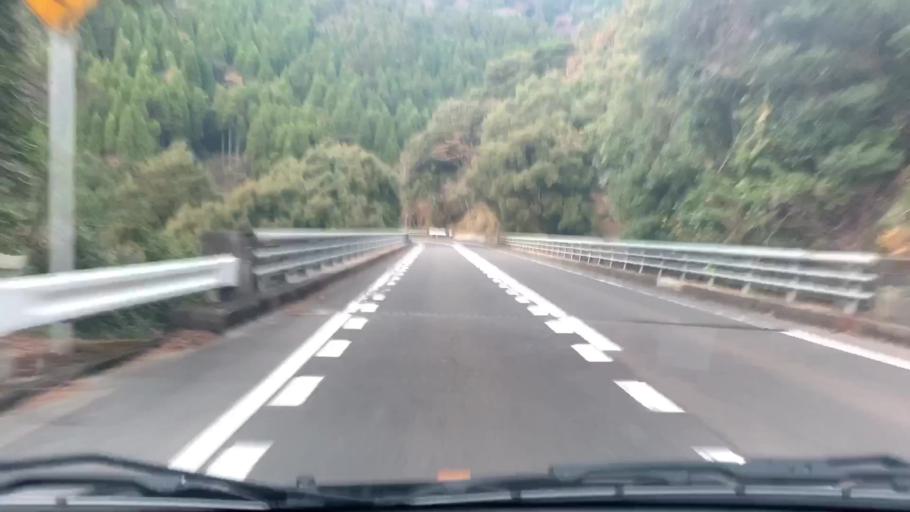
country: JP
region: Nagasaki
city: Omura
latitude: 32.9840
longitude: 130.0358
